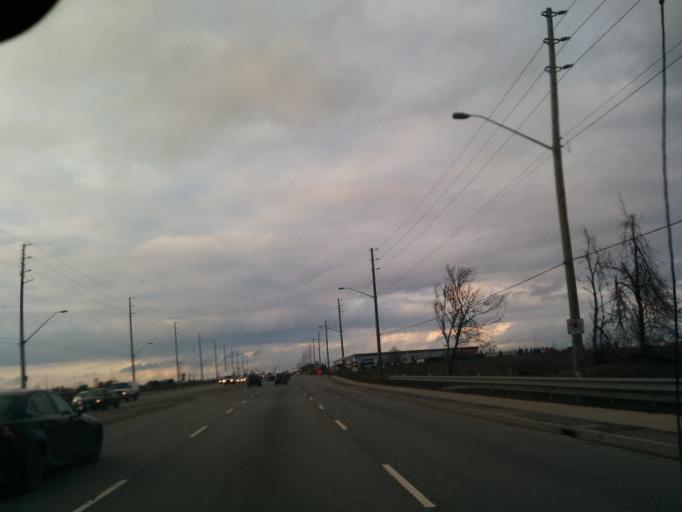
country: CA
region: Ontario
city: Brampton
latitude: 43.7985
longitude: -79.6665
